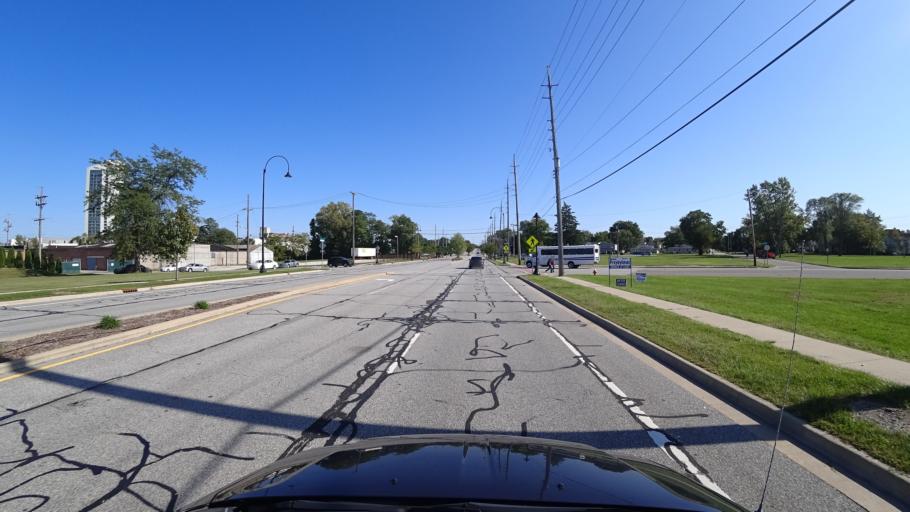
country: US
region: Indiana
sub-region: LaPorte County
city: Michigan City
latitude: 41.7189
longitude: -86.8977
